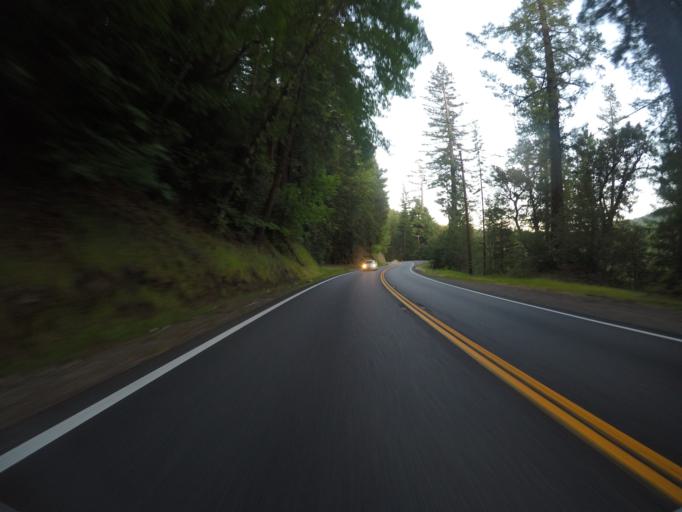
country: US
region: California
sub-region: Humboldt County
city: Redway
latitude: 39.9148
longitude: -123.7611
